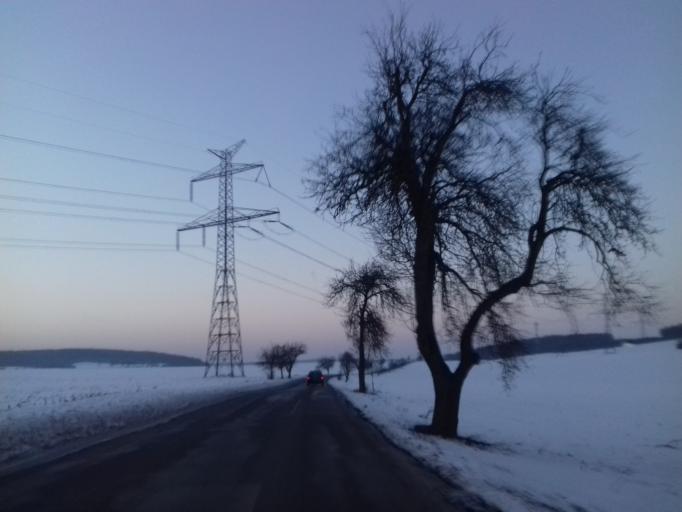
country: CZ
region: Central Bohemia
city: Revnice
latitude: 49.9414
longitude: 14.2280
